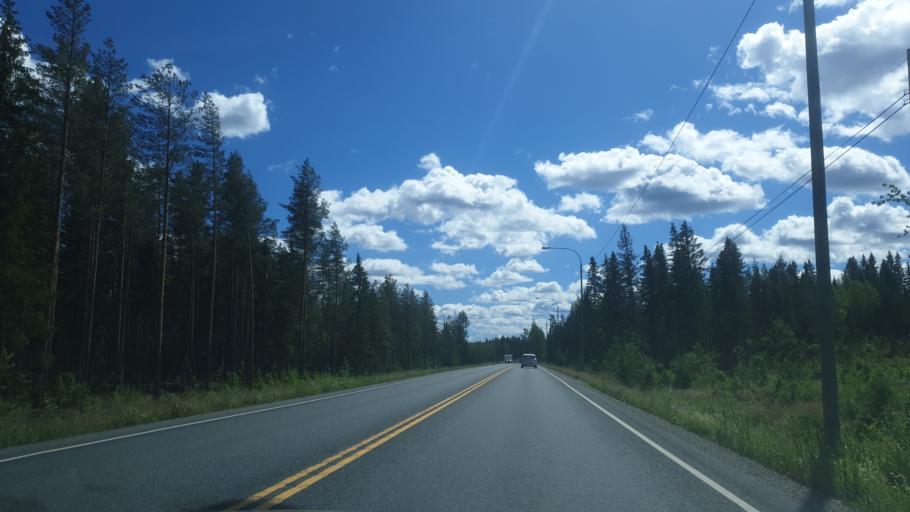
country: FI
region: Northern Savo
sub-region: Varkaus
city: Leppaevirta
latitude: 62.5430
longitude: 27.6289
